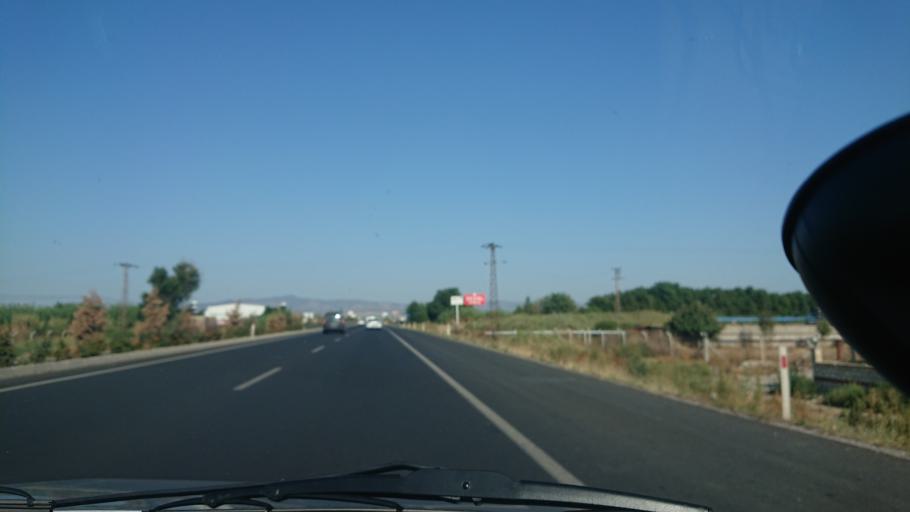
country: TR
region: Manisa
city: Salihli
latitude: 38.5022
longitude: 28.2136
